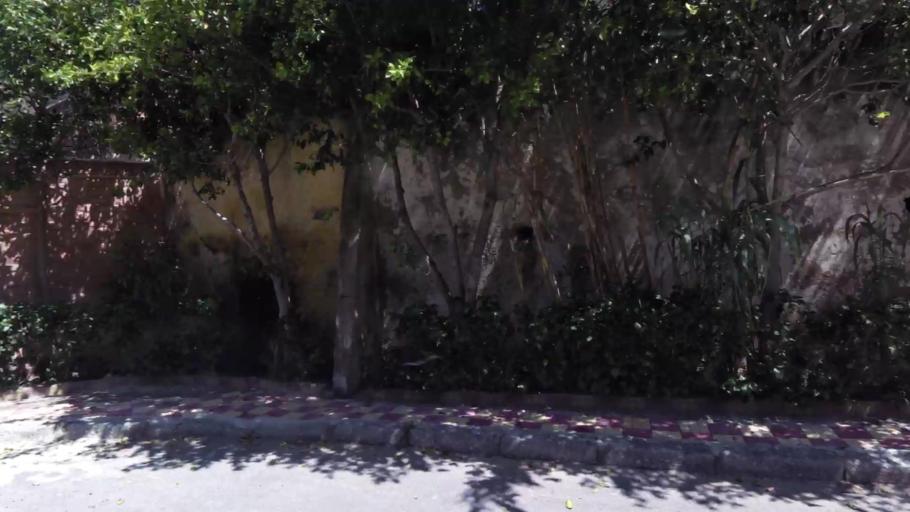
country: MA
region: Tanger-Tetouan
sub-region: Tanger-Assilah
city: Tangier
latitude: 35.7776
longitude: -5.8285
